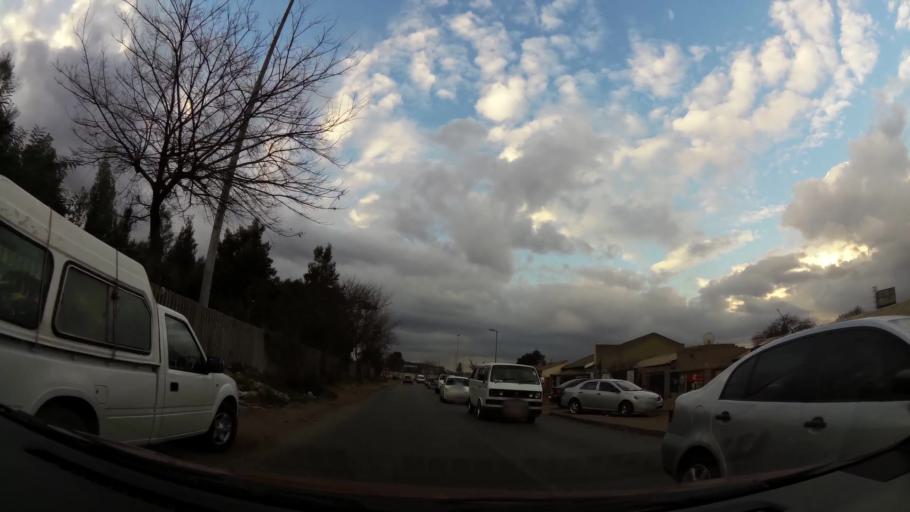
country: ZA
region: Gauteng
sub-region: City of Johannesburg Metropolitan Municipality
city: Soweto
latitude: -26.2455
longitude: 27.8318
